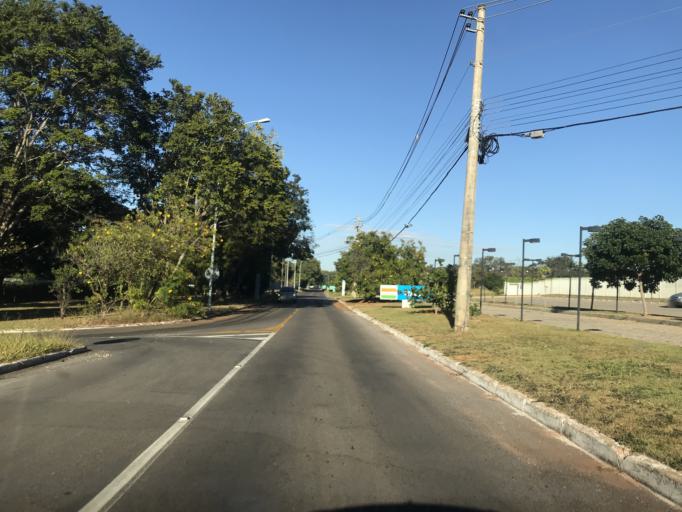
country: BR
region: Federal District
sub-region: Brasilia
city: Brasilia
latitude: -15.8197
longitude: -47.8866
